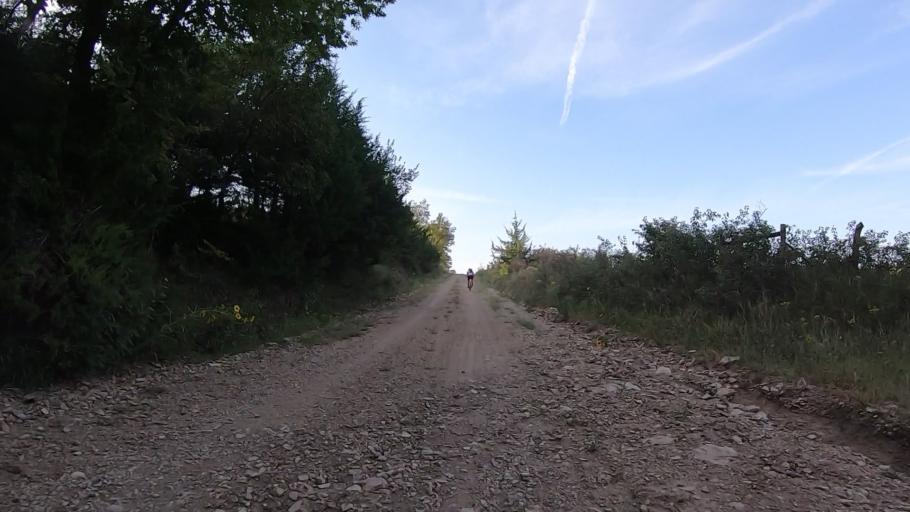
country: US
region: Kansas
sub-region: Marshall County
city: Blue Rapids
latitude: 39.7541
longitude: -96.7506
